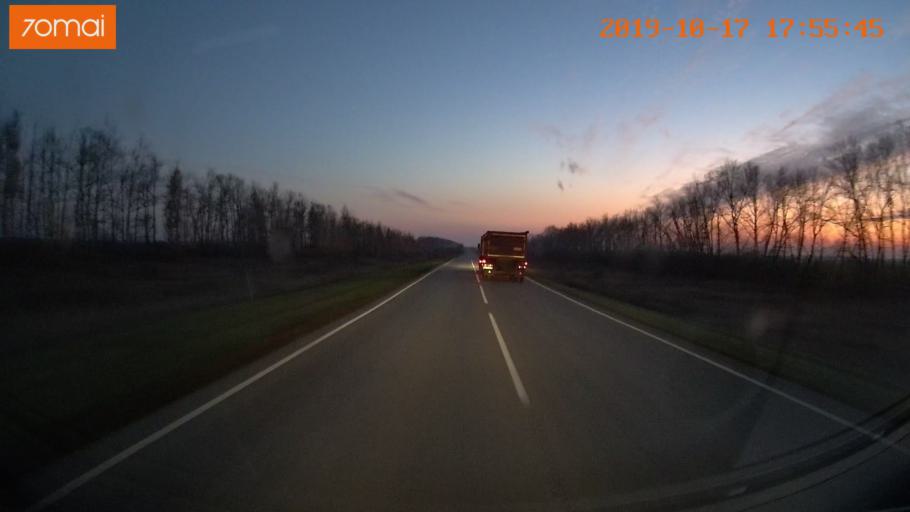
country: RU
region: Tula
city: Kurkino
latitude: 53.5899
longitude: 38.6553
